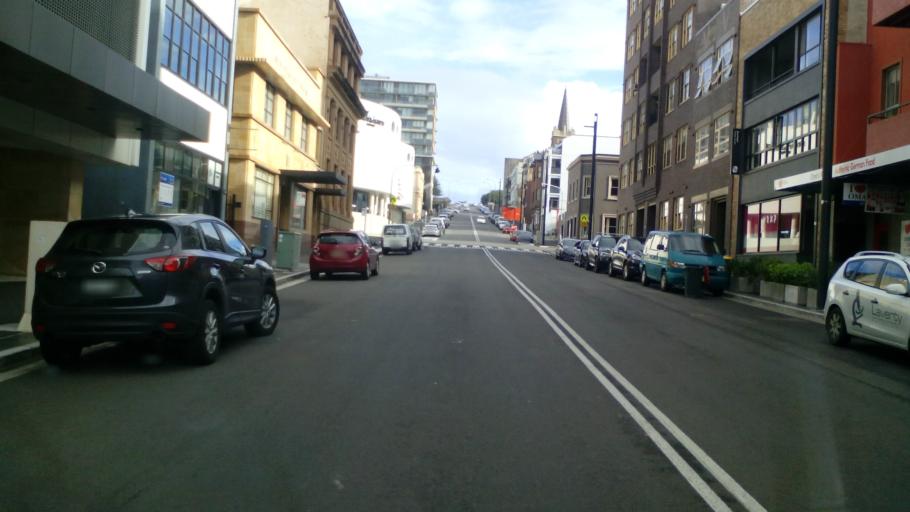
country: AU
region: New South Wales
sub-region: Newcastle
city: Newcastle
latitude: -32.9281
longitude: 151.7842
